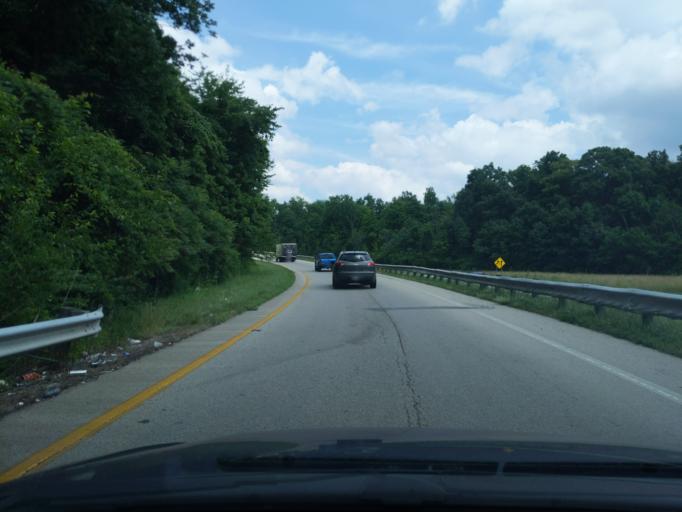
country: US
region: Ohio
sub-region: Hamilton County
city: Highpoint
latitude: 39.2698
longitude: -84.3490
